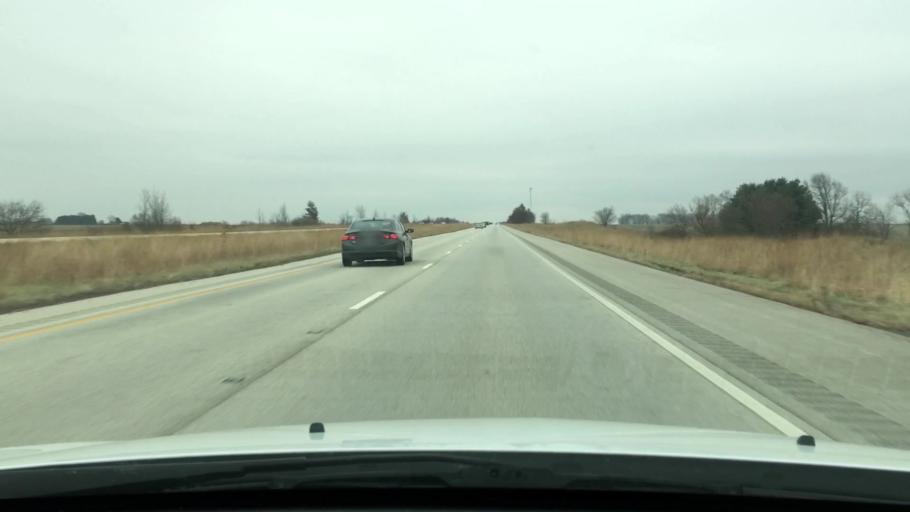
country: US
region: Illinois
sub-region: Sangamon County
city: New Berlin
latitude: 39.7404
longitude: -89.8878
